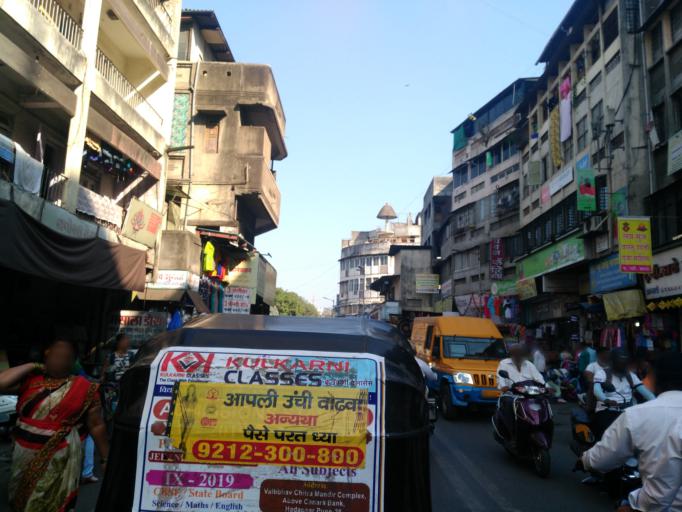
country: IN
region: Maharashtra
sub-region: Pune Division
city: Pune
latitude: 18.5134
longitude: 73.8544
